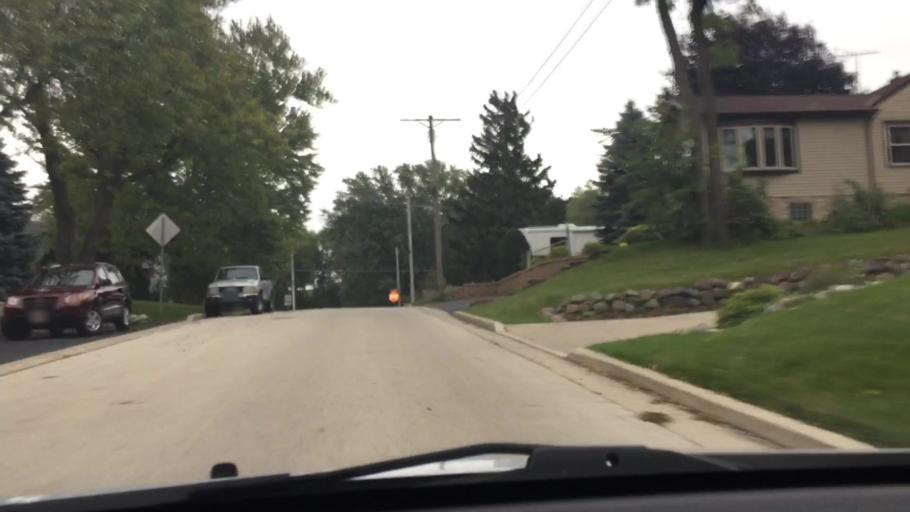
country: US
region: Wisconsin
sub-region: Waukesha County
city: Pewaukee
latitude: 43.0775
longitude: -88.2671
